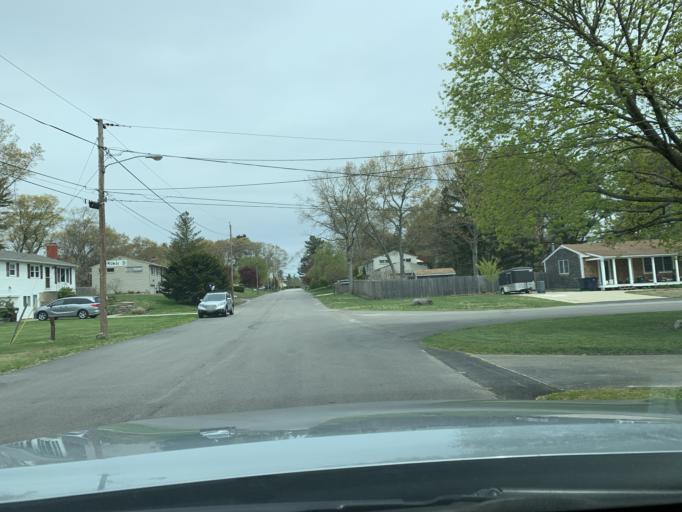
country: US
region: Rhode Island
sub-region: Washington County
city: North Kingstown
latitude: 41.6008
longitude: -71.4849
